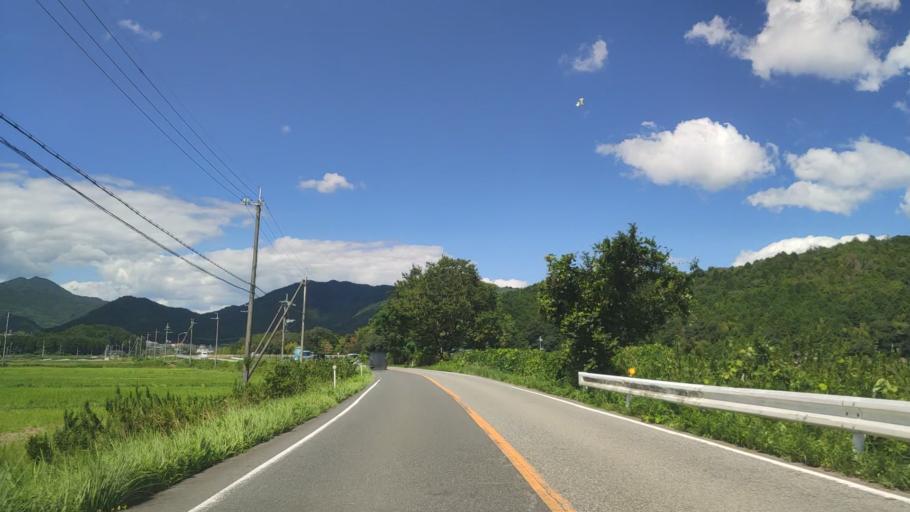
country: JP
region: Kyoto
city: Fukuchiyama
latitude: 35.1874
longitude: 135.1236
